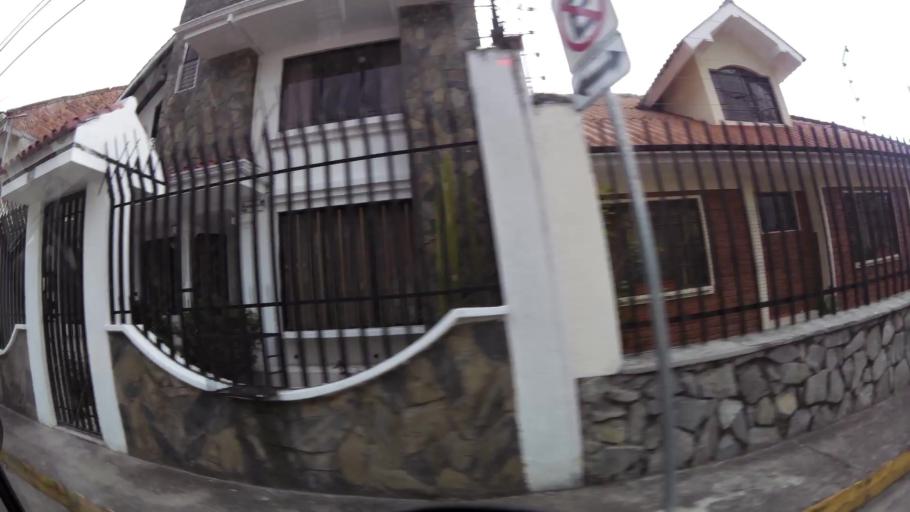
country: EC
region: Azuay
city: Cuenca
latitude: -2.8895
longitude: -79.0207
